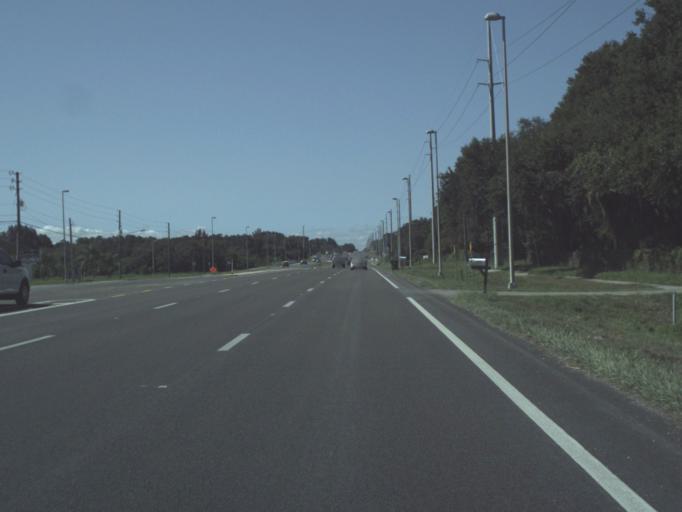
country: US
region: Florida
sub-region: Hillsborough County
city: Sun City Center
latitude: 27.7770
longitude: -82.3351
